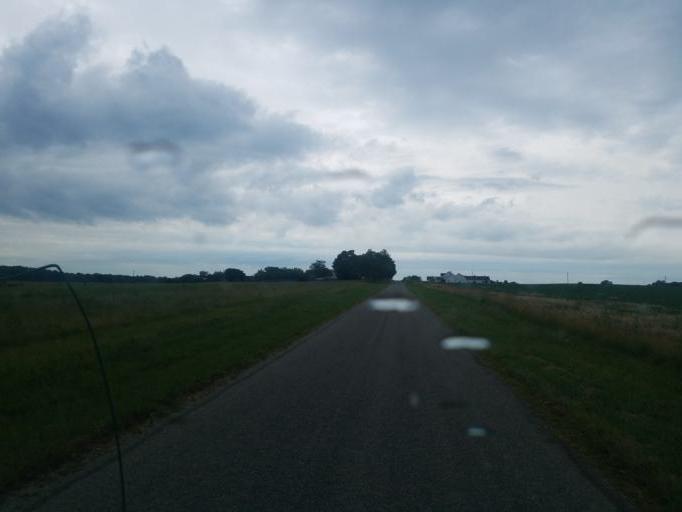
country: US
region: Ohio
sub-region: Defiance County
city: Hicksville
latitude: 41.3681
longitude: -84.7734
